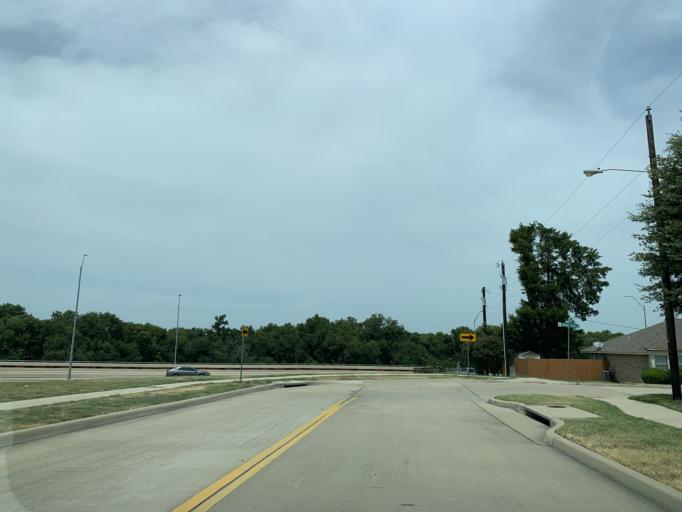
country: US
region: Texas
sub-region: Dallas County
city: Grand Prairie
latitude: 32.6638
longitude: -97.0277
